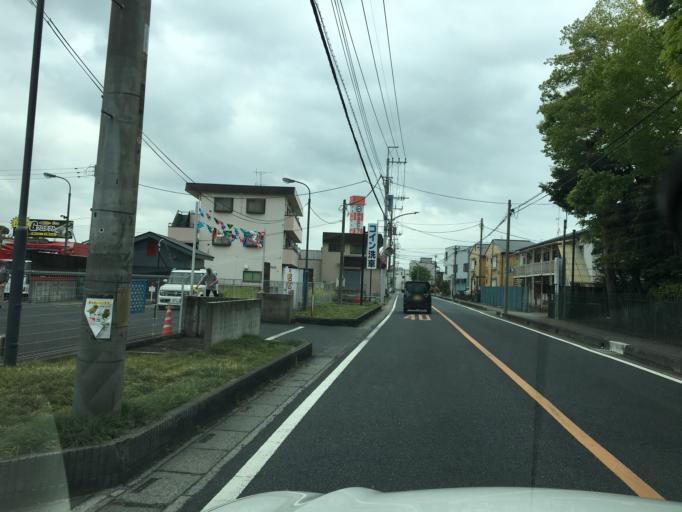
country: JP
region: Saitama
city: Koshigaya
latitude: 35.8637
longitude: 139.7815
